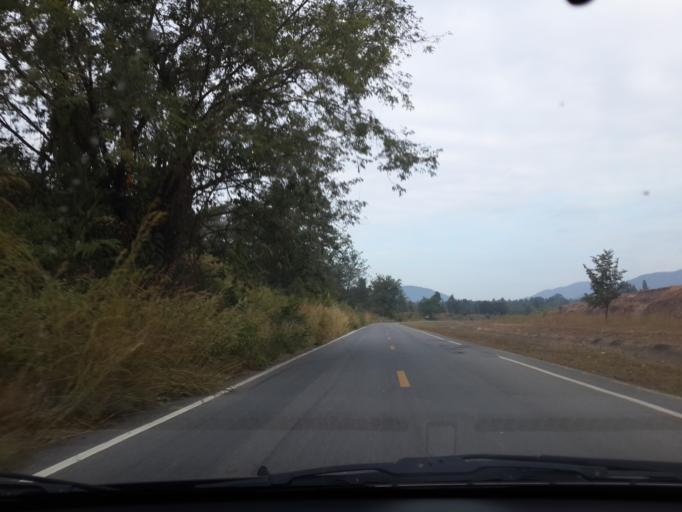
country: TH
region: Chiang Mai
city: San Sai
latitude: 18.8953
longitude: 99.1496
